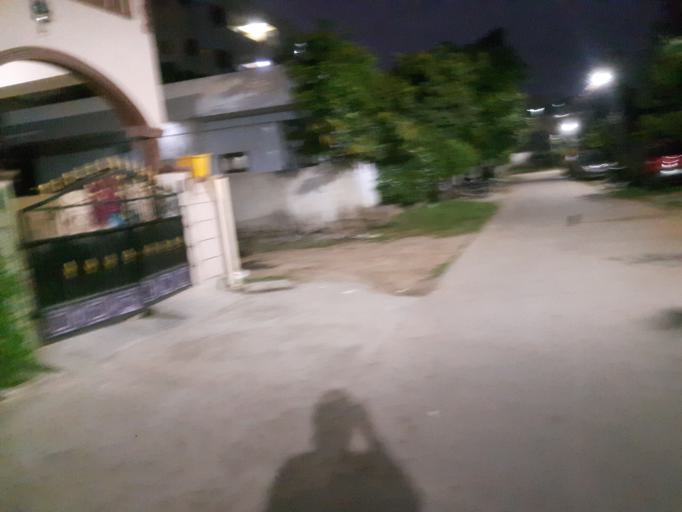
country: IN
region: Telangana
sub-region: Rangareddi
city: Quthbullapur
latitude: 17.4973
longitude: 78.4670
